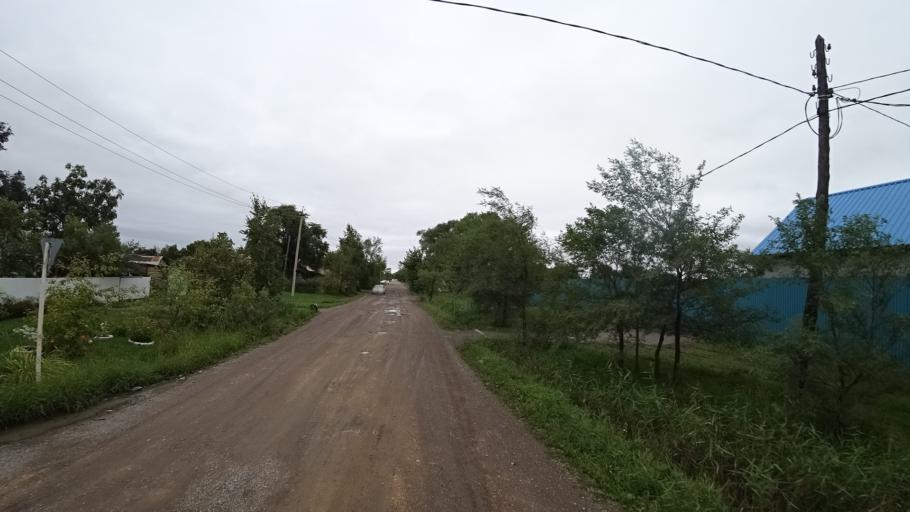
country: RU
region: Primorskiy
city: Chernigovka
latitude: 44.3464
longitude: 132.5623
